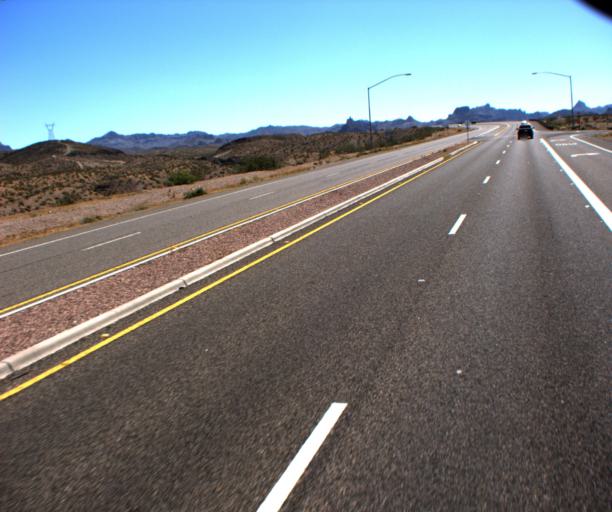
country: US
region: Nevada
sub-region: Clark County
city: Laughlin
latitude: 35.1859
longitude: -114.5016
